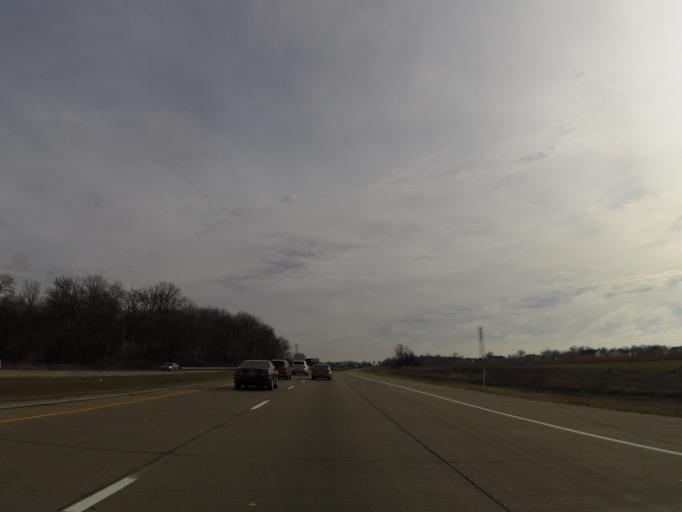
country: US
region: Indiana
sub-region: Marion County
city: Warren Park
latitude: 39.7316
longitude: -86.0313
